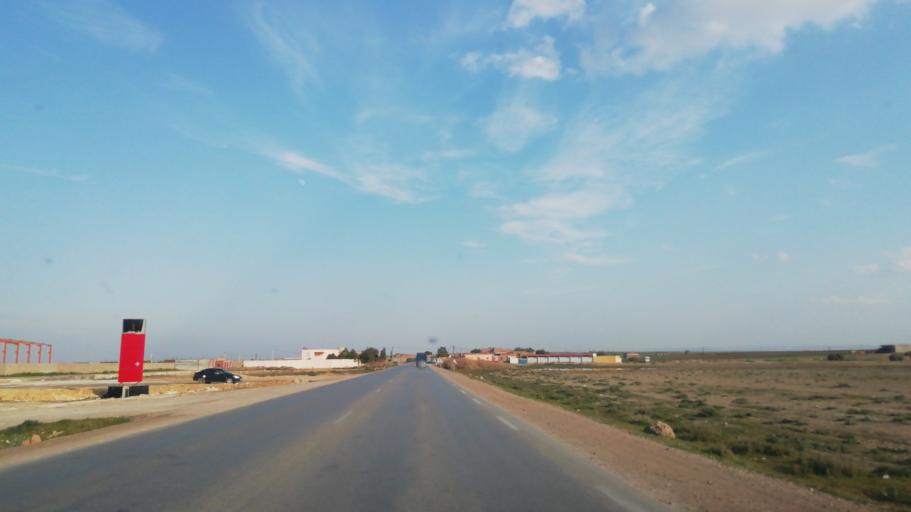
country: DZ
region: Relizane
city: Relizane
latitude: 35.8980
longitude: 0.5834
